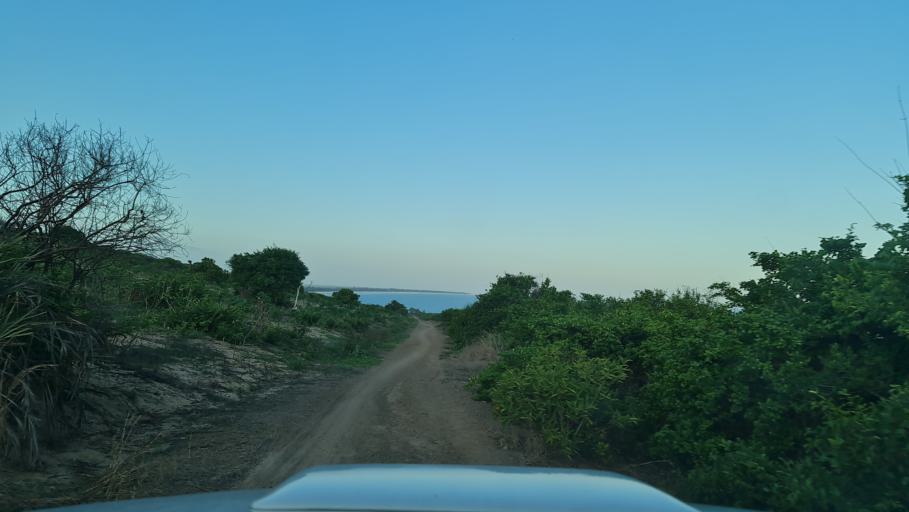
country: MZ
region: Nampula
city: Ilha de Mocambique
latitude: -15.6330
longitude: 40.4177
